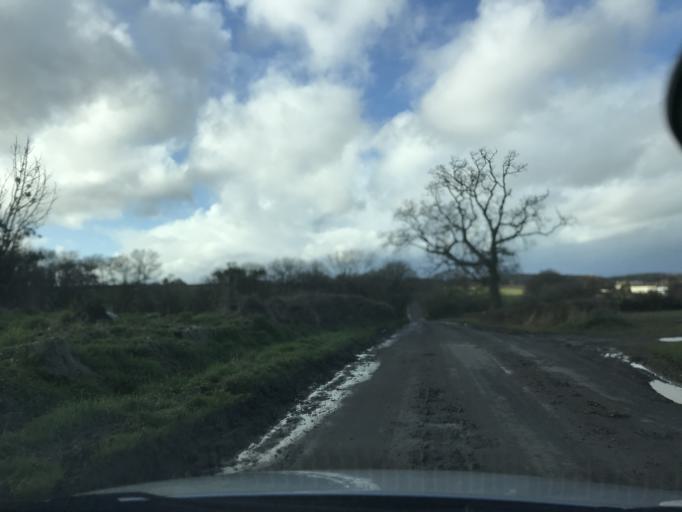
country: GB
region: England
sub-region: Somerset
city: Creech Saint Michael
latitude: 50.9552
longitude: -3.0156
